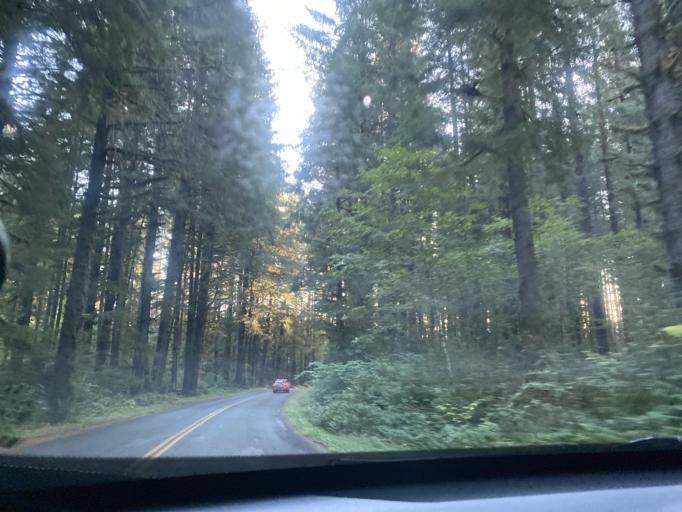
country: US
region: Washington
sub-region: Clallam County
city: Forks
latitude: 47.8091
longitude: -124.0999
